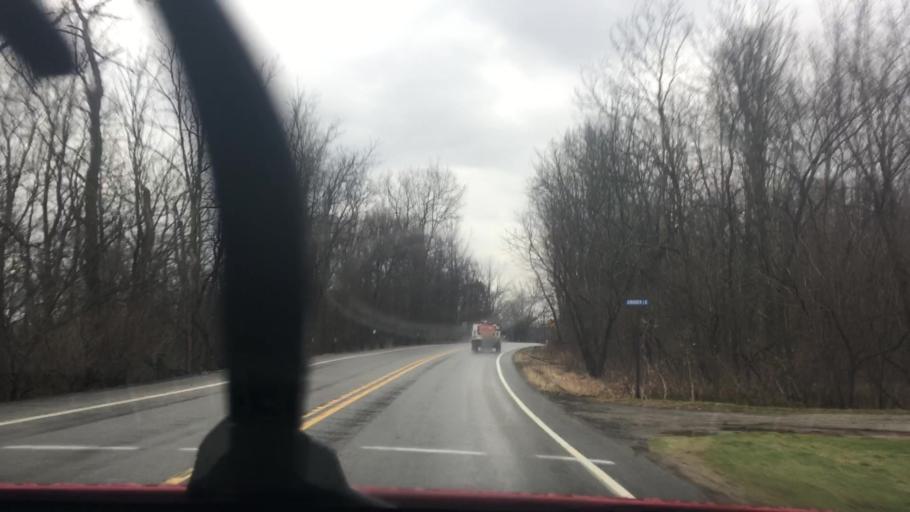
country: US
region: Pennsylvania
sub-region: Washington County
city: McDonald
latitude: 40.3323
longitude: -80.2369
